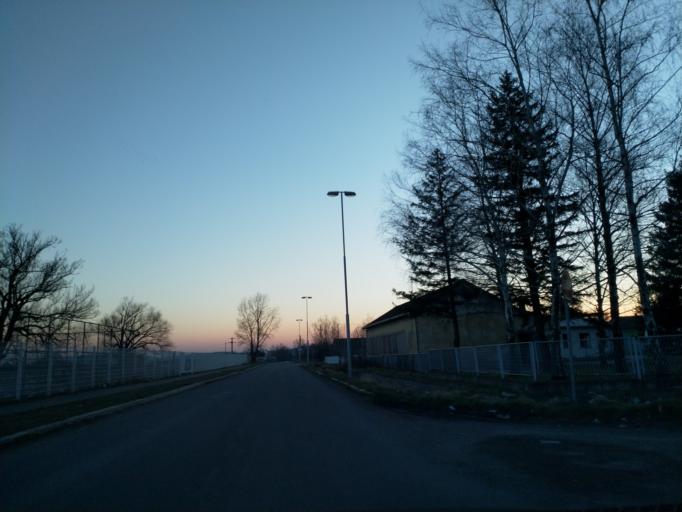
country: RS
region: Central Serbia
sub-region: Pomoravski Okrug
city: Paracin
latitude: 43.9056
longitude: 21.5025
